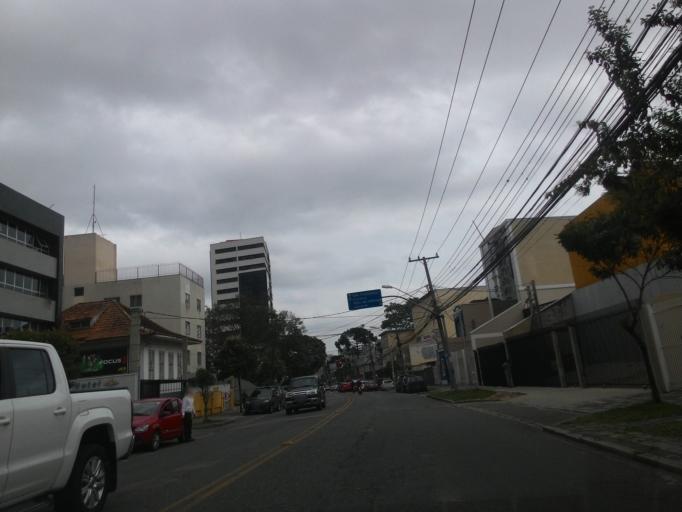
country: BR
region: Parana
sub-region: Curitiba
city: Curitiba
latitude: -25.4158
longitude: -49.2715
